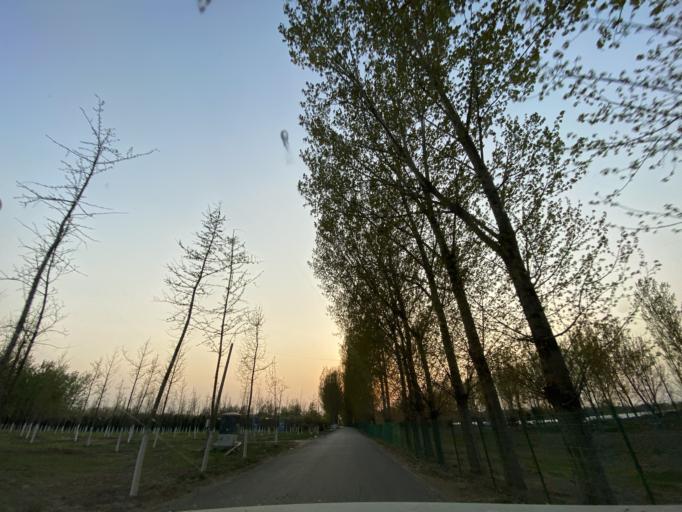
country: CN
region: Beijing
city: Weishanzhuang
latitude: 39.6064
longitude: 116.4130
